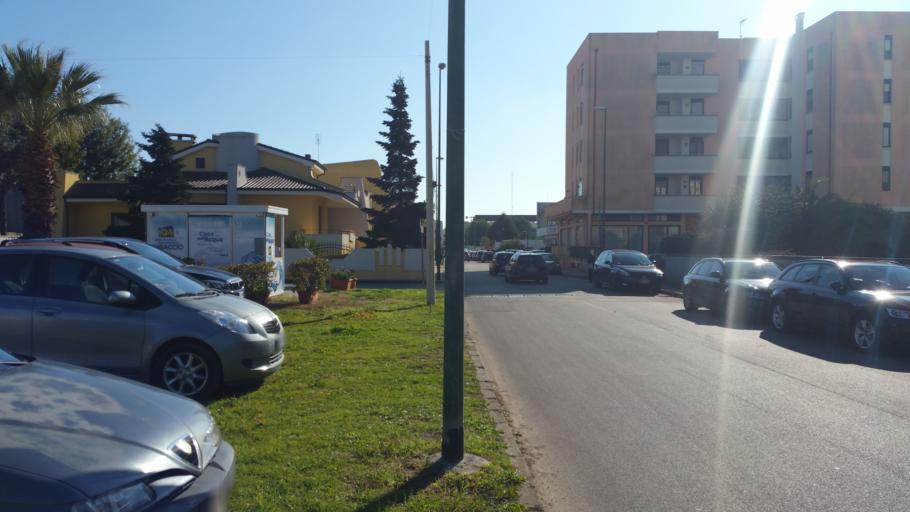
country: IT
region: Apulia
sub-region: Provincia di Lecce
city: Tricase
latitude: 39.9266
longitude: 18.3549
